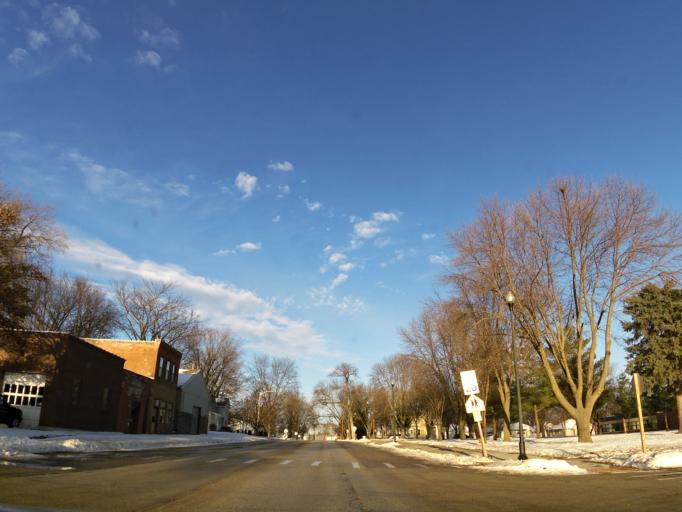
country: US
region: Iowa
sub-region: Butler County
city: Shell Rock
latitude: 42.7122
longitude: -92.5808
